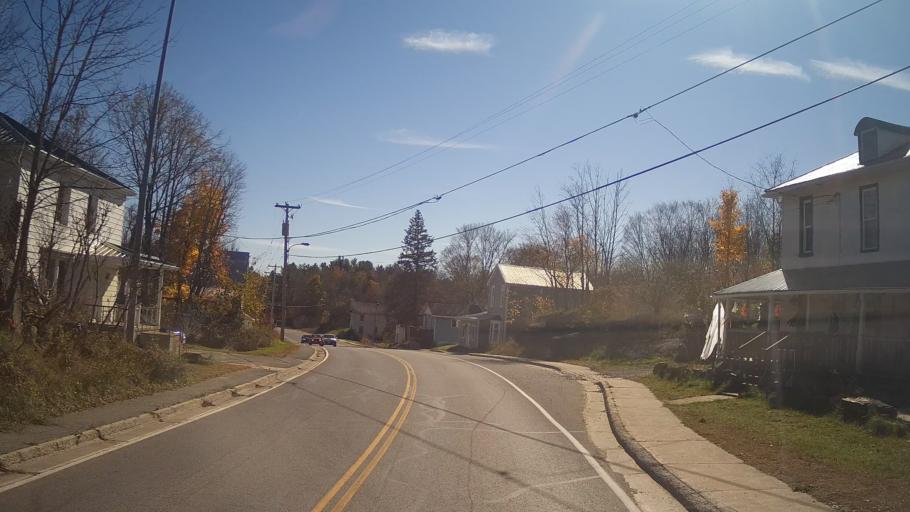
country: CA
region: Ontario
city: Skatepark
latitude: 44.6559
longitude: -76.7163
